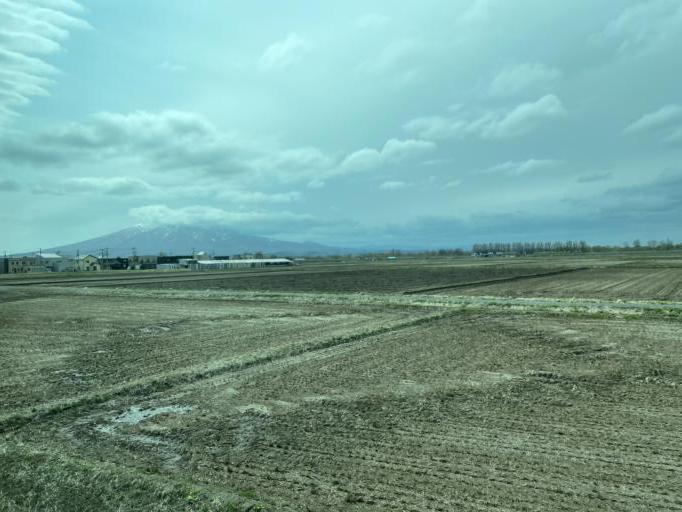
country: JP
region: Aomori
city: Goshogawara
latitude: 40.7719
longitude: 140.4339
